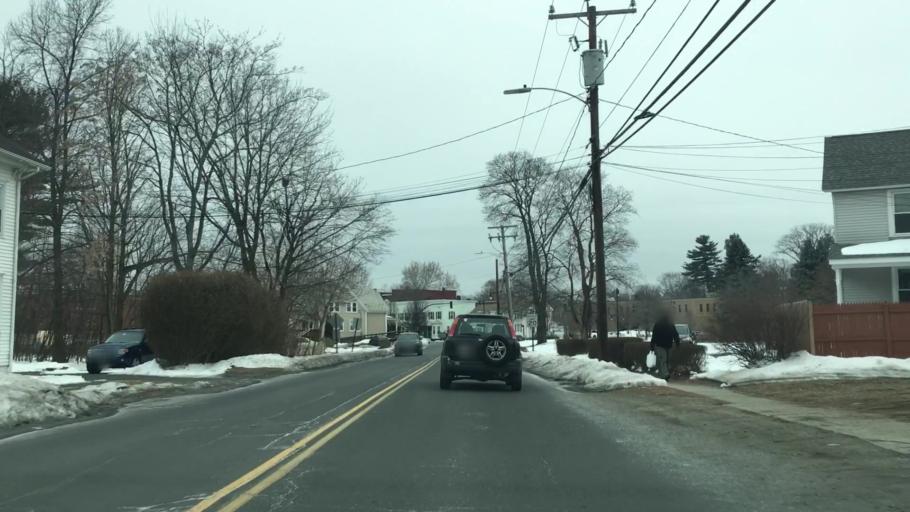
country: US
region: Massachusetts
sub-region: Hampden County
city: Westfield
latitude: 42.1311
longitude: -72.7419
